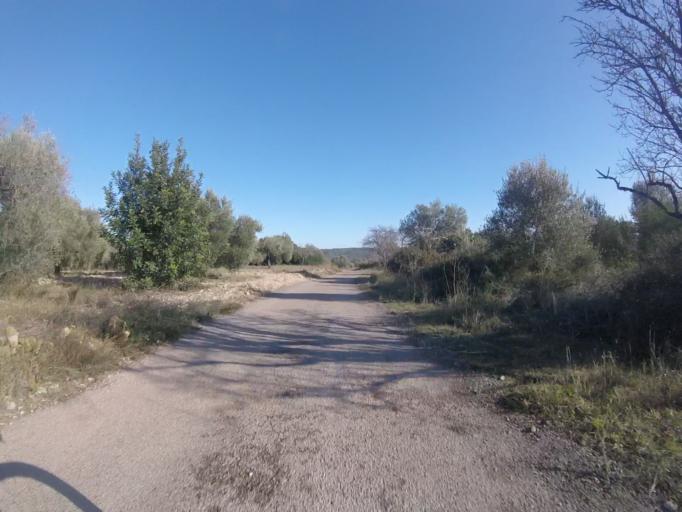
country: ES
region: Valencia
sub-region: Provincia de Castello
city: Cuevas de Vinroma
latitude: 40.2901
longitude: 0.0884
